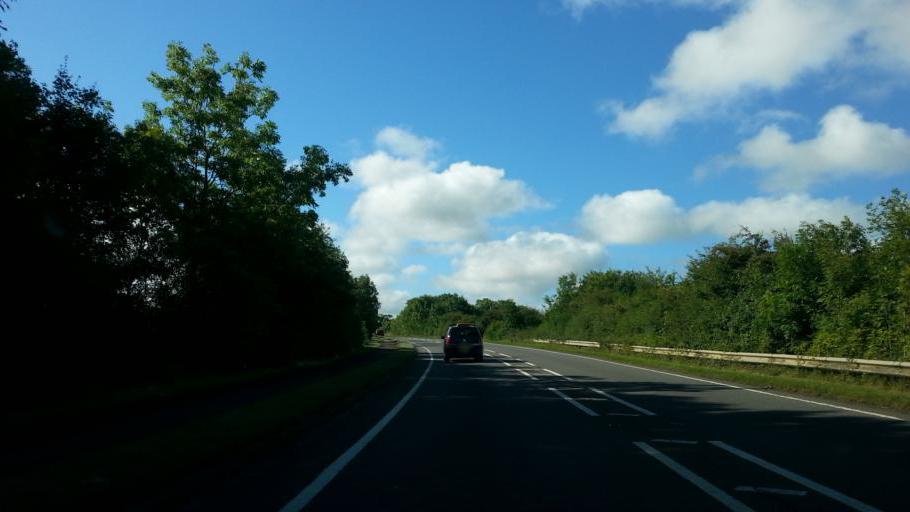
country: GB
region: England
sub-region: Northamptonshire
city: Broughton
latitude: 52.3568
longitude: -0.7907
